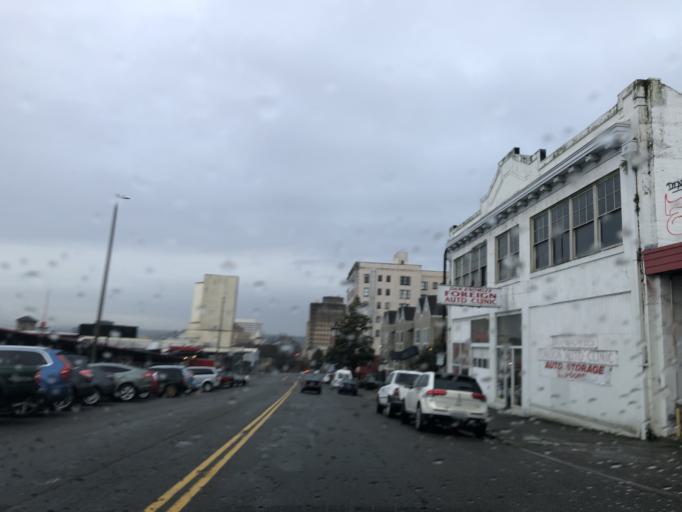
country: US
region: Washington
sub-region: Pierce County
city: Tacoma
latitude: 47.2600
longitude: -122.4443
